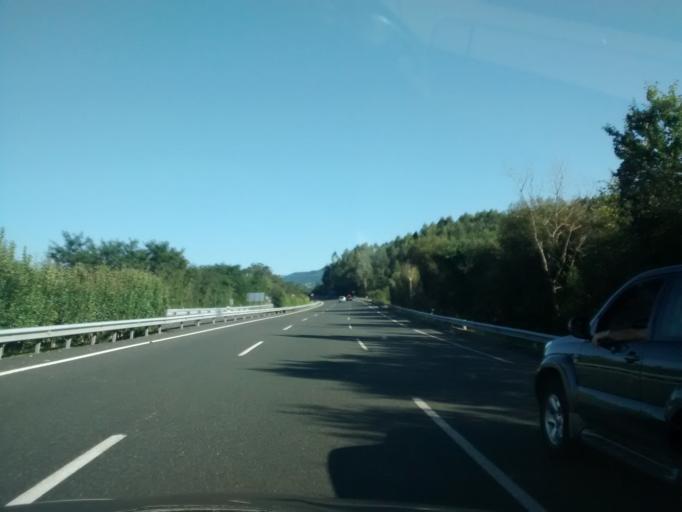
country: ES
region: Cantabria
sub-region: Provincia de Cantabria
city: Luzmela
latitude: 43.3251
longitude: -4.1869
